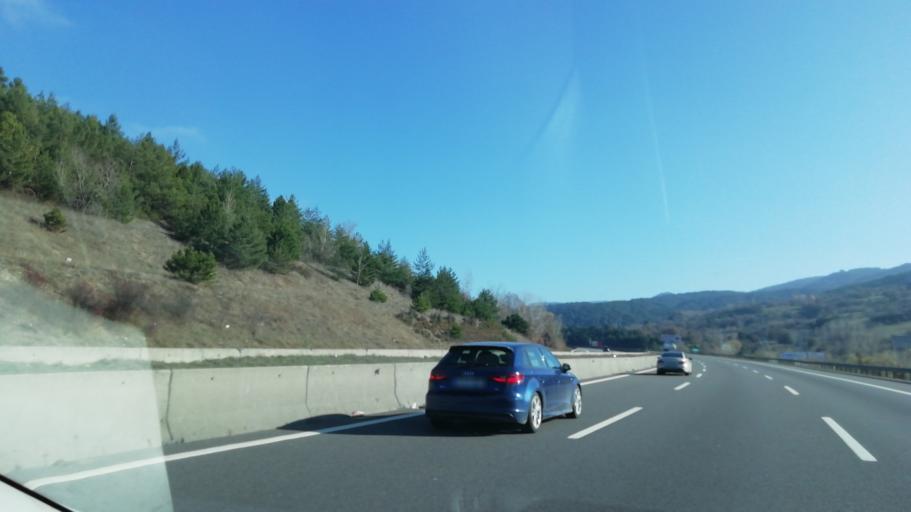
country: TR
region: Bolu
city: Bolu
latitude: 40.7345
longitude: 31.8041
